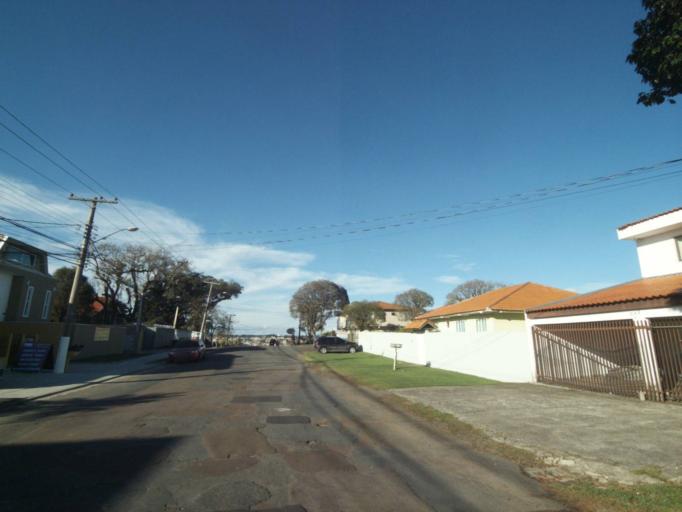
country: BR
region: Parana
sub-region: Curitiba
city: Curitiba
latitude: -25.3895
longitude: -49.2555
